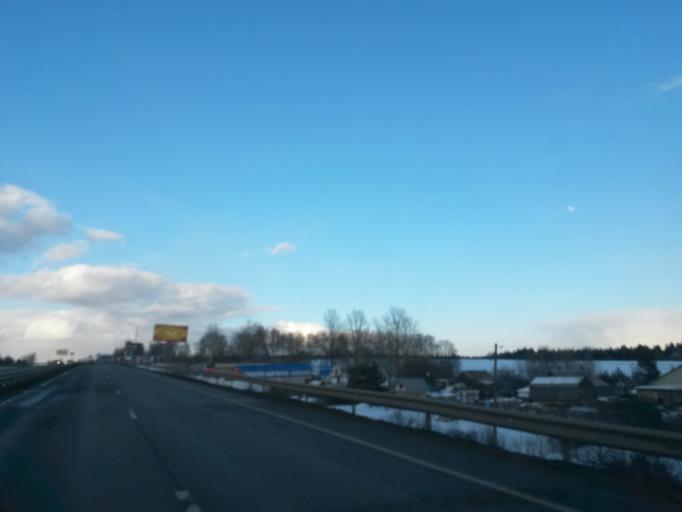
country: RU
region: Moskovskaya
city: Semkhoz
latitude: 56.2077
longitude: 38.0703
